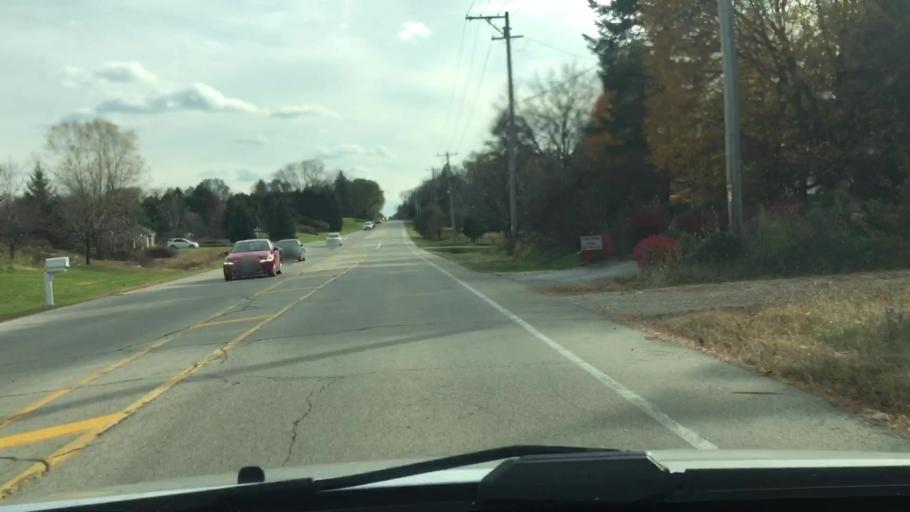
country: US
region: Wisconsin
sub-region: Waukesha County
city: Delafield
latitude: 43.0739
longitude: -88.4037
